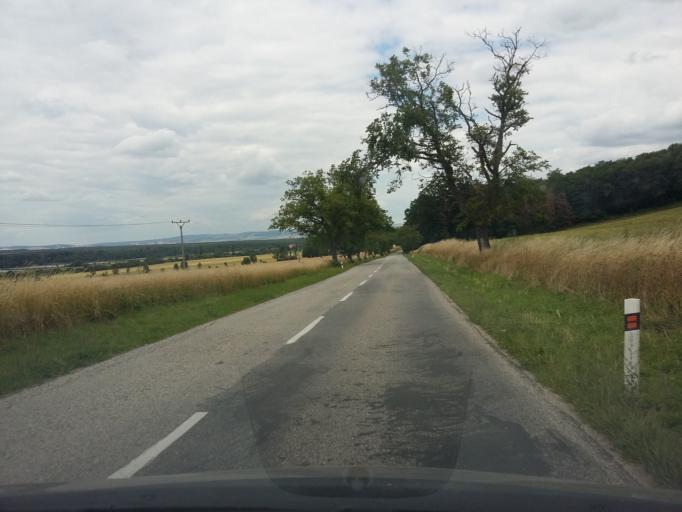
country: SK
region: Trnavsky
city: Smolenice
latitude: 48.5671
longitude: 17.3465
